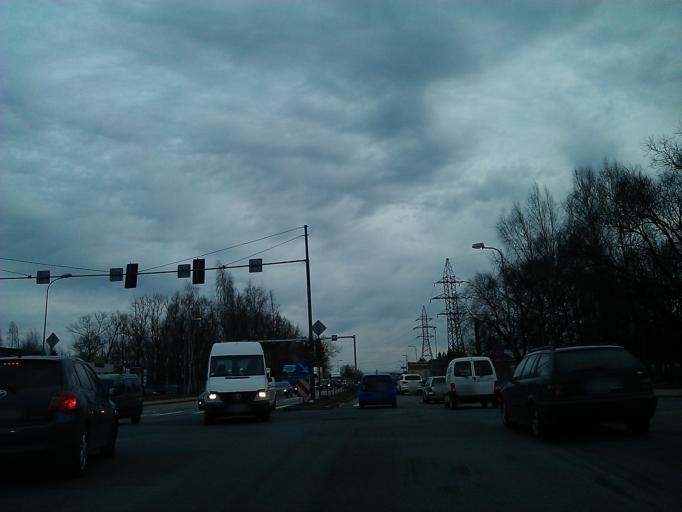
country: LV
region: Riga
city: Riga
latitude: 56.9395
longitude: 24.1720
